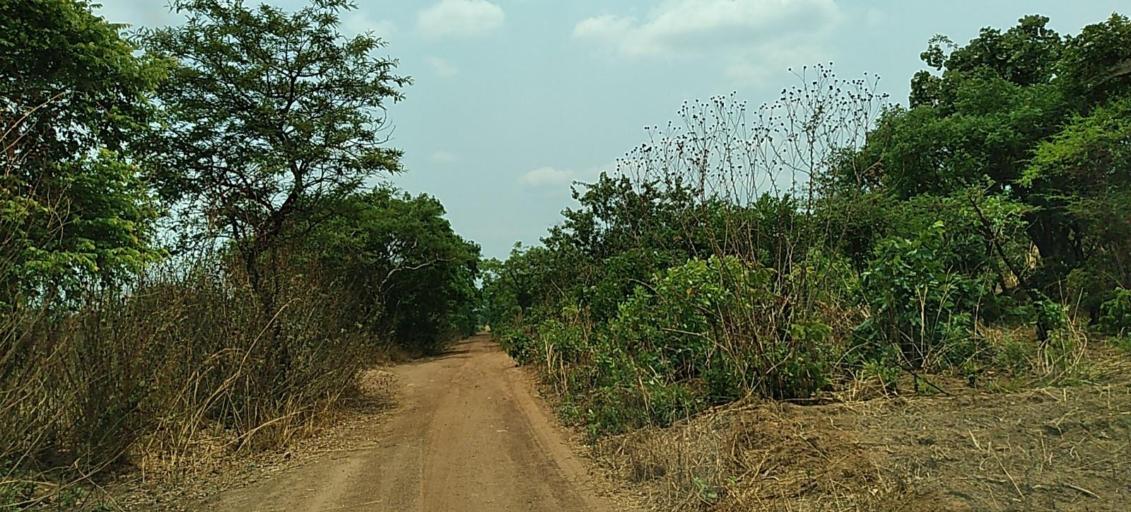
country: ZM
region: Copperbelt
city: Kalulushi
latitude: -12.7991
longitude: 28.0056
